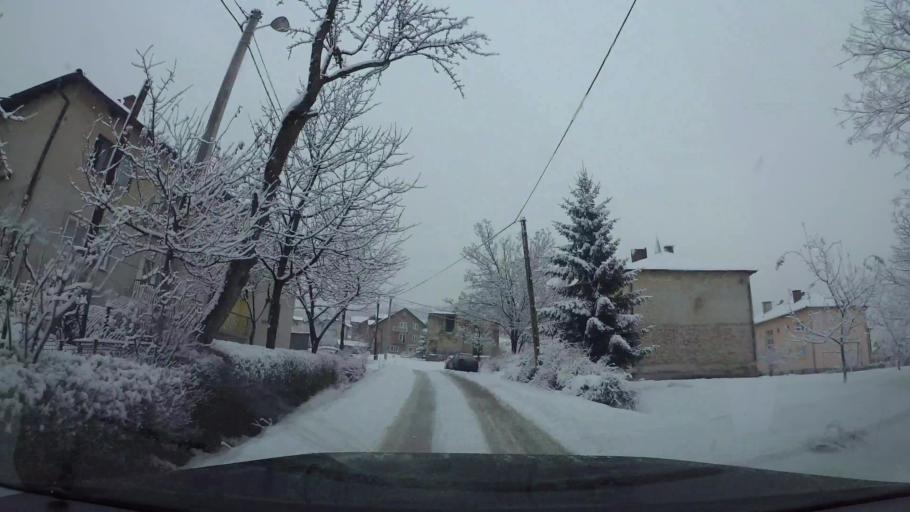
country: BA
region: Federation of Bosnia and Herzegovina
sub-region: Kanton Sarajevo
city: Sarajevo
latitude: 43.8610
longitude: 18.3208
